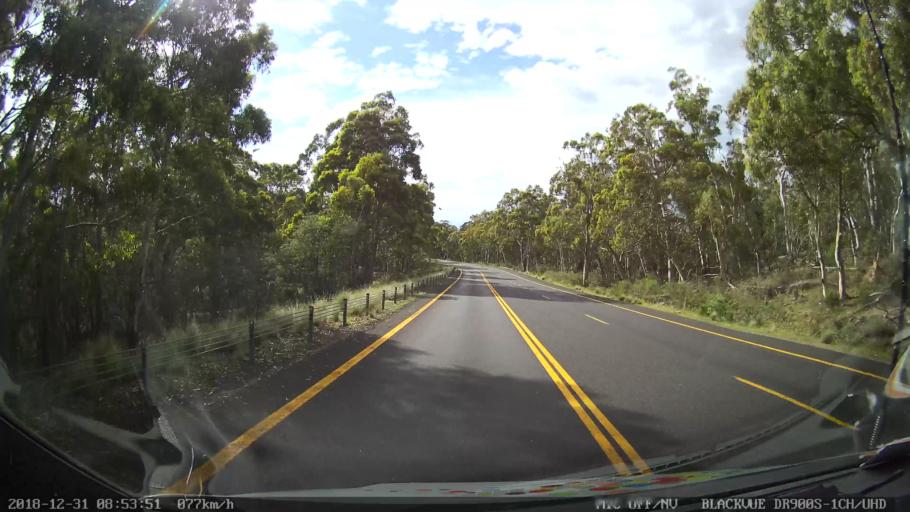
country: AU
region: New South Wales
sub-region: Snowy River
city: Jindabyne
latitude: -36.3510
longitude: 148.5536
